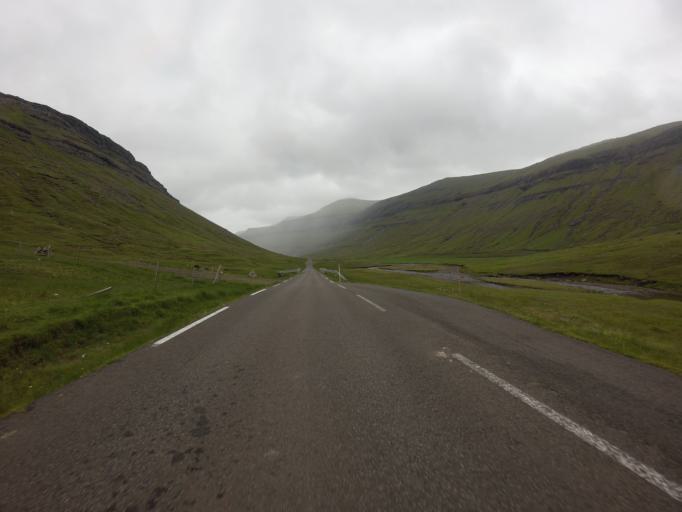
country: FO
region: Streymoy
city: Vestmanna
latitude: 62.2260
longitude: -7.1321
